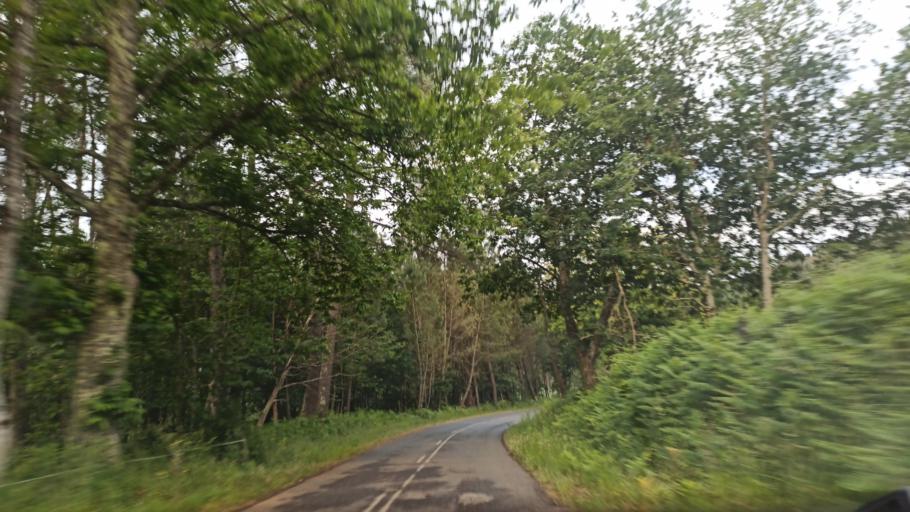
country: ES
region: Galicia
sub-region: Provincia da Coruna
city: Santiso
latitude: 42.8177
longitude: -8.1407
